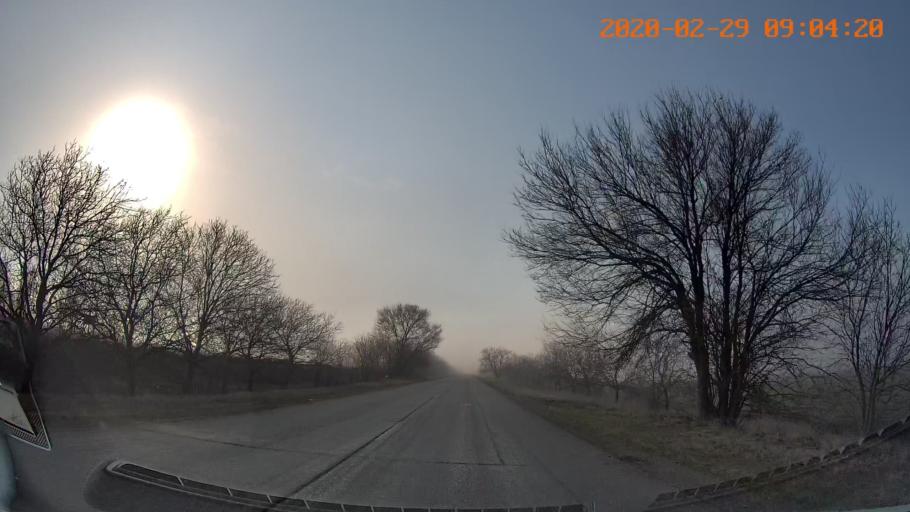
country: MD
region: Telenesti
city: Tiraspolul Nou
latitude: 46.9040
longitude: 29.7356
